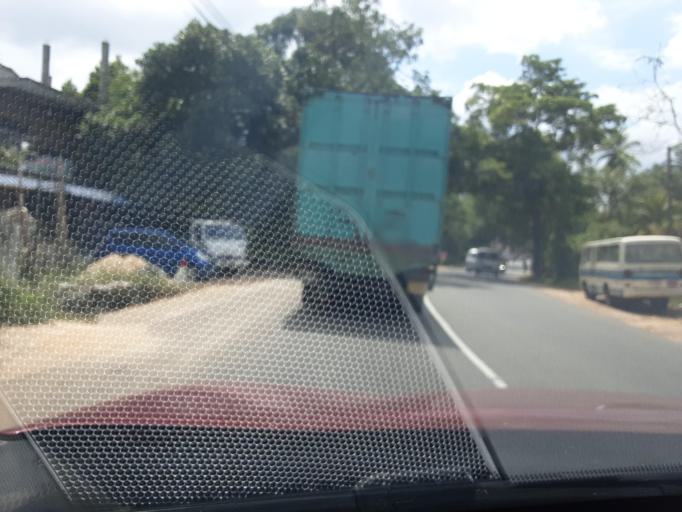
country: LK
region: North Western
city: Kuliyapitiya
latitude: 7.4504
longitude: 80.1970
